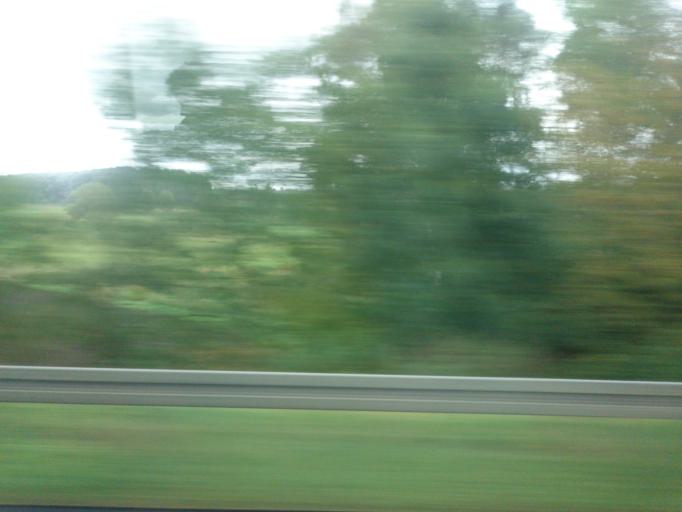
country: DE
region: Saxony-Anhalt
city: Kotzschau
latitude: 51.3011
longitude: 12.1498
